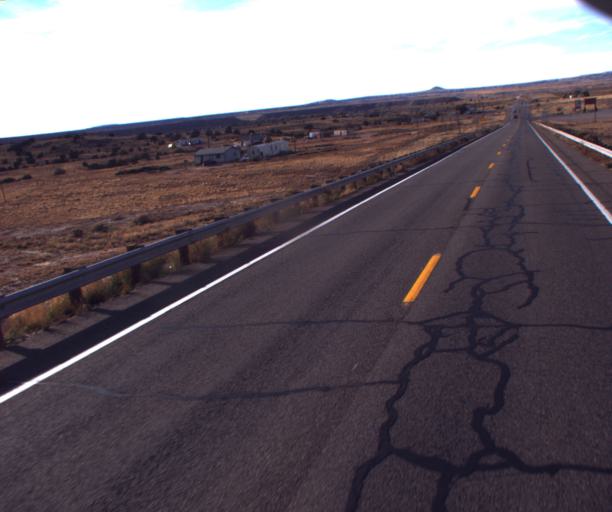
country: US
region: New Mexico
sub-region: San Juan County
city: Shiprock
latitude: 36.9177
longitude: -109.0816
